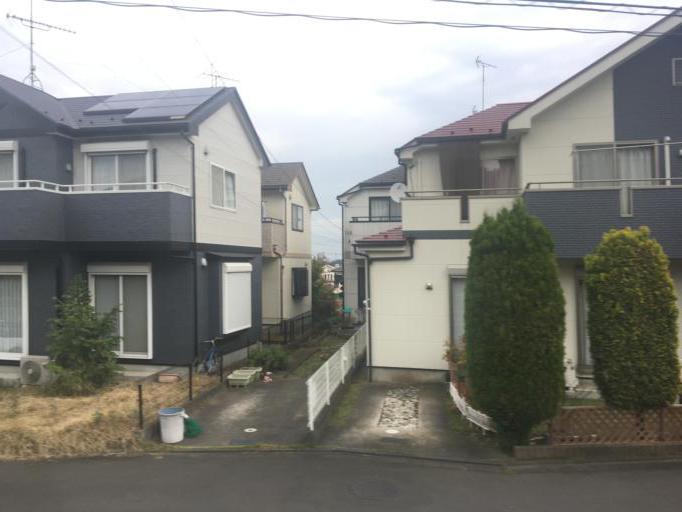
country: JP
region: Tokyo
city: Hino
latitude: 35.6874
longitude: 139.3670
